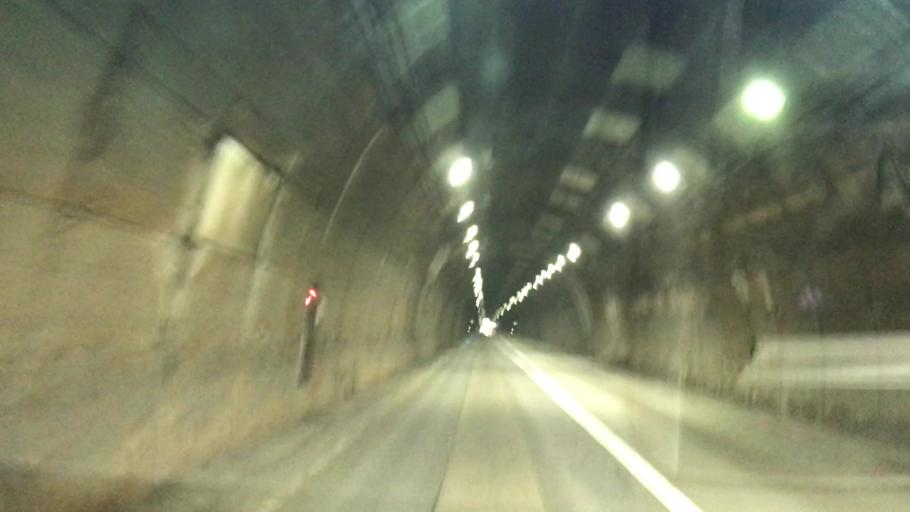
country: JP
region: Hokkaido
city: Yoichi
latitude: 43.0603
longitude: 140.6858
